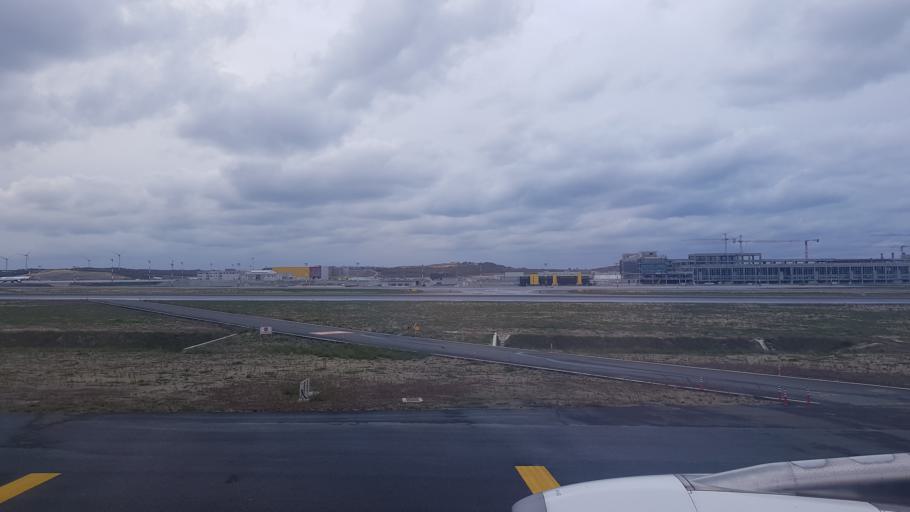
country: TR
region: Istanbul
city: Durusu
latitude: 41.2740
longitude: 28.7297
